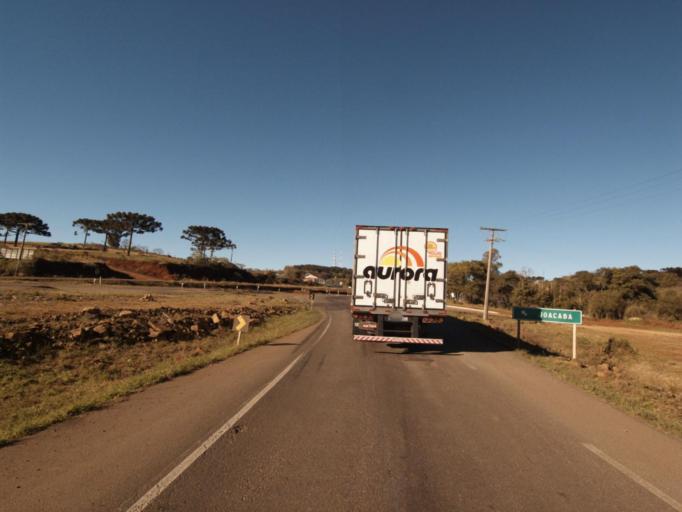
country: BR
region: Santa Catarina
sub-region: Xanxere
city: Xanxere
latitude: -26.8855
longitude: -52.4345
